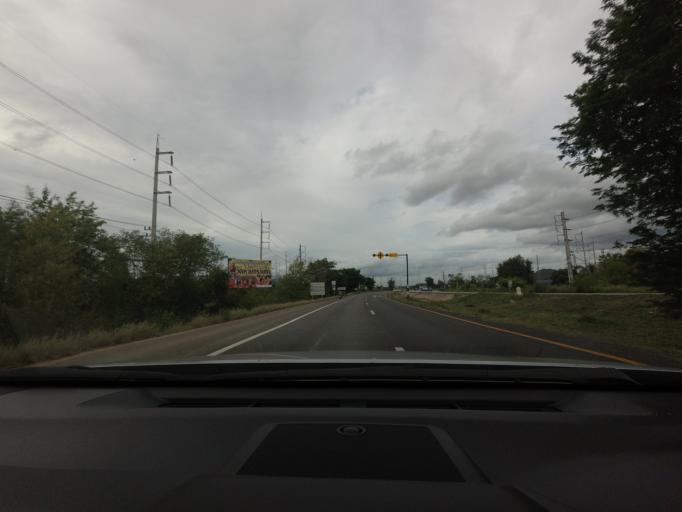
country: TH
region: Prachuap Khiri Khan
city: Hua Hin
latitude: 12.6749
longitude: 99.8815
